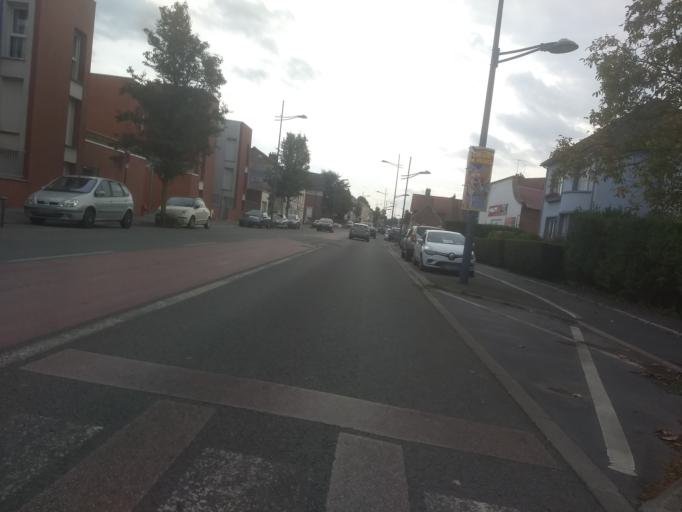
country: FR
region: Nord-Pas-de-Calais
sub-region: Departement du Pas-de-Calais
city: Beaurains
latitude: 50.2725
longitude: 2.7840
